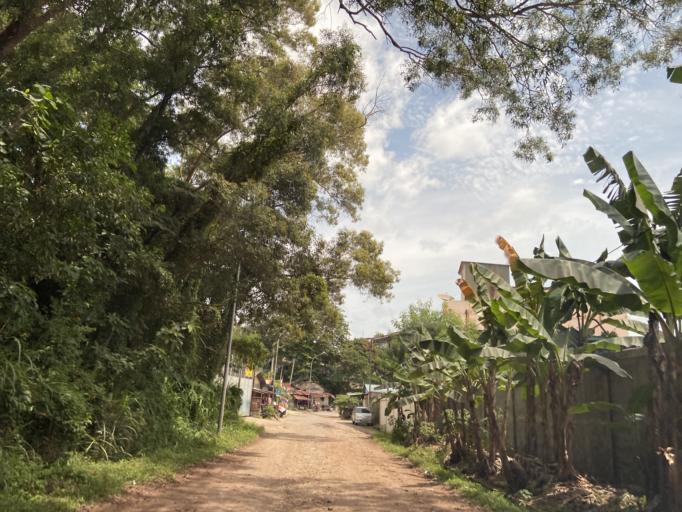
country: SG
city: Singapore
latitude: 1.1607
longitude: 104.0067
